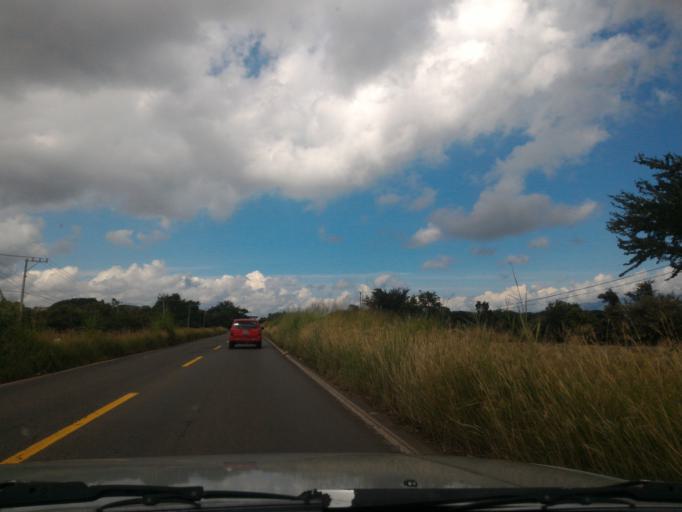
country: MX
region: Jalisco
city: Amatitan
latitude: 20.8479
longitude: -103.7530
